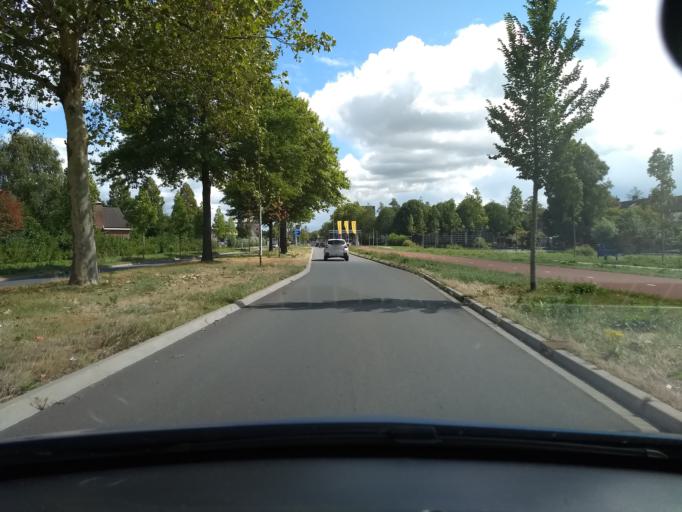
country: NL
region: South Holland
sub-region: Gemeente Papendrecht
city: Papendrecht
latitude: 51.8373
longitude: 4.6876
